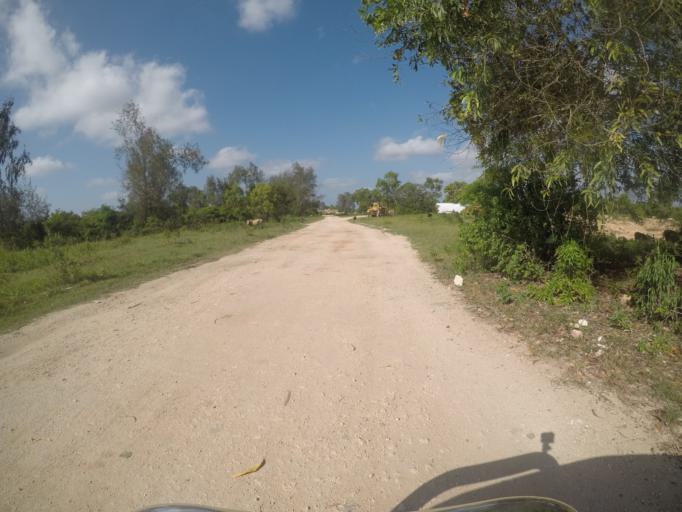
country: TZ
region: Zanzibar Central/South
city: Koani
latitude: -6.2175
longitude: 39.3324
